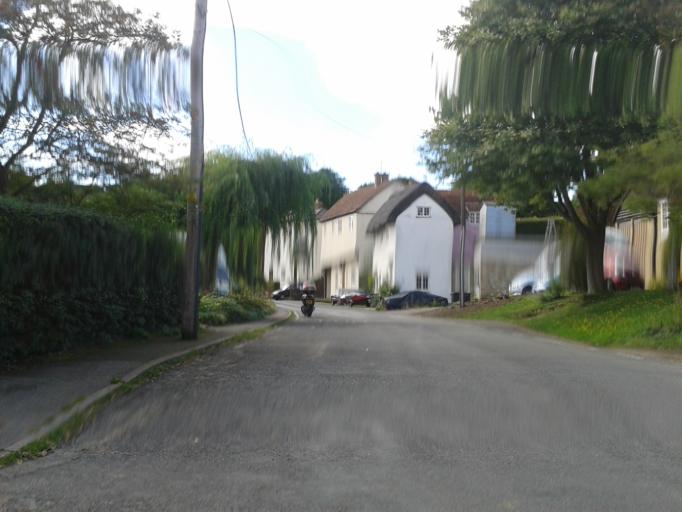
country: GB
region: England
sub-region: Cambridgeshire
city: Duxford
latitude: 52.0365
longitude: 0.1321
